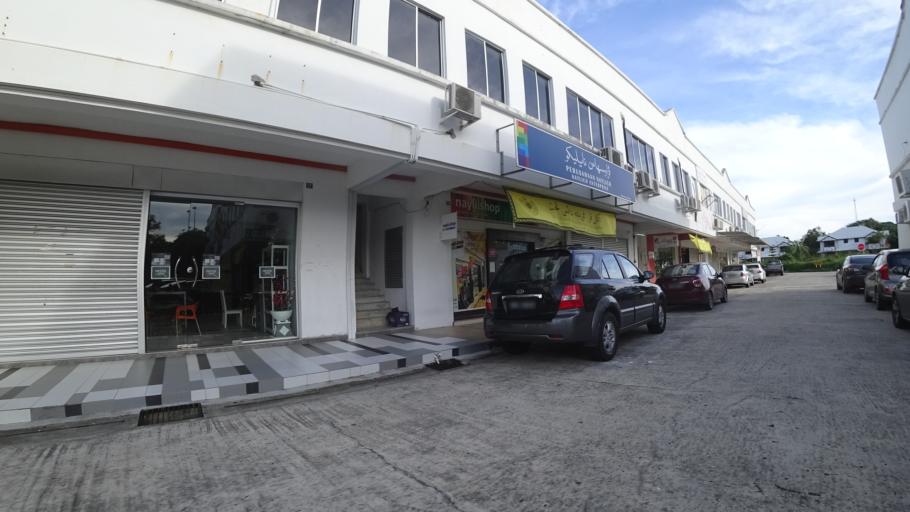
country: BN
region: Brunei and Muara
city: Bandar Seri Begawan
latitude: 4.8932
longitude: 114.8380
